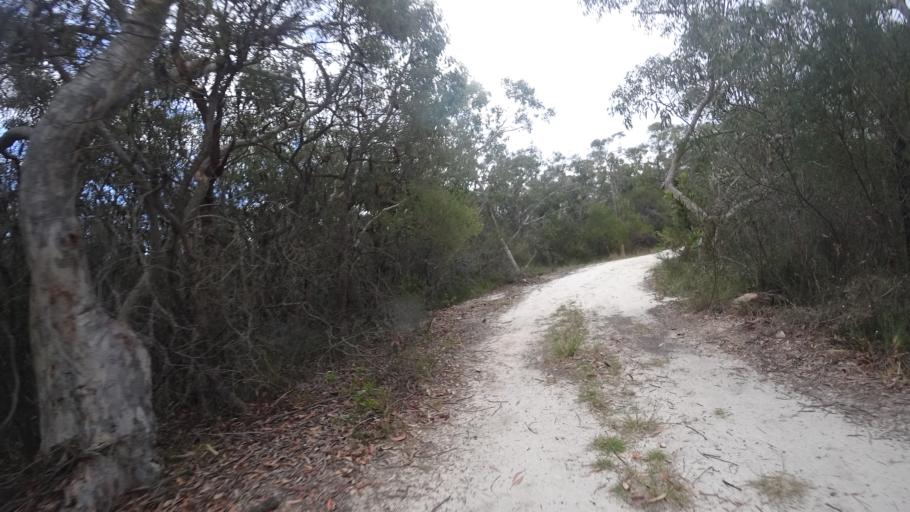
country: AU
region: New South Wales
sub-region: Warringah
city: Davidson
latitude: -33.7001
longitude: 151.2003
